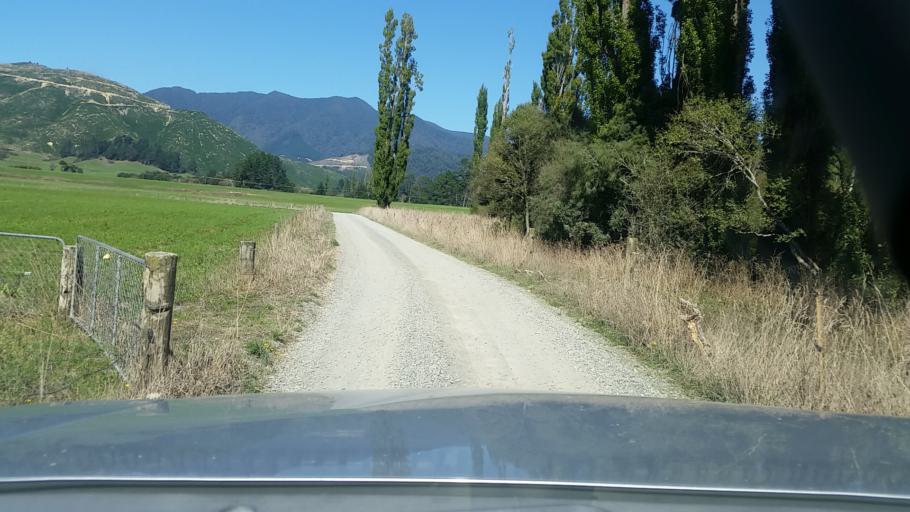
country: NZ
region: Nelson
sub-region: Nelson City
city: Nelson
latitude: -41.2684
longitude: 173.5755
